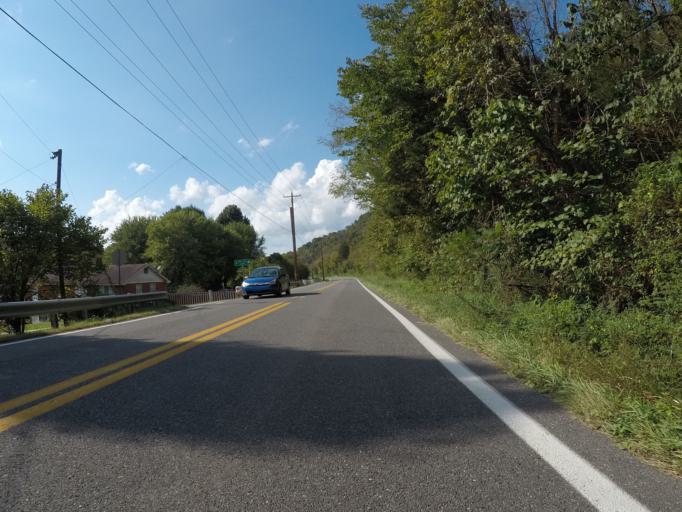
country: US
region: West Virginia
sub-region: Wayne County
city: Lavalette
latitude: 38.3508
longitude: -82.4980
